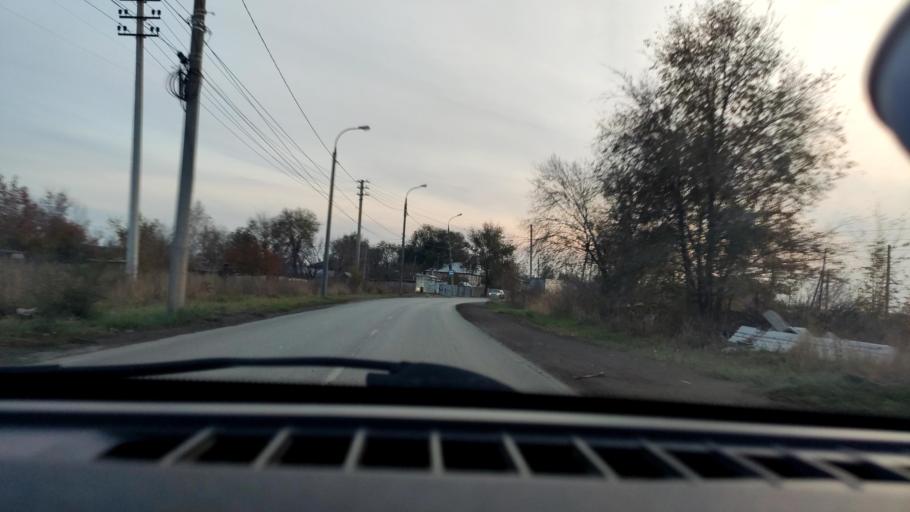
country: RU
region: Samara
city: Samara
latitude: 53.1430
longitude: 50.1329
